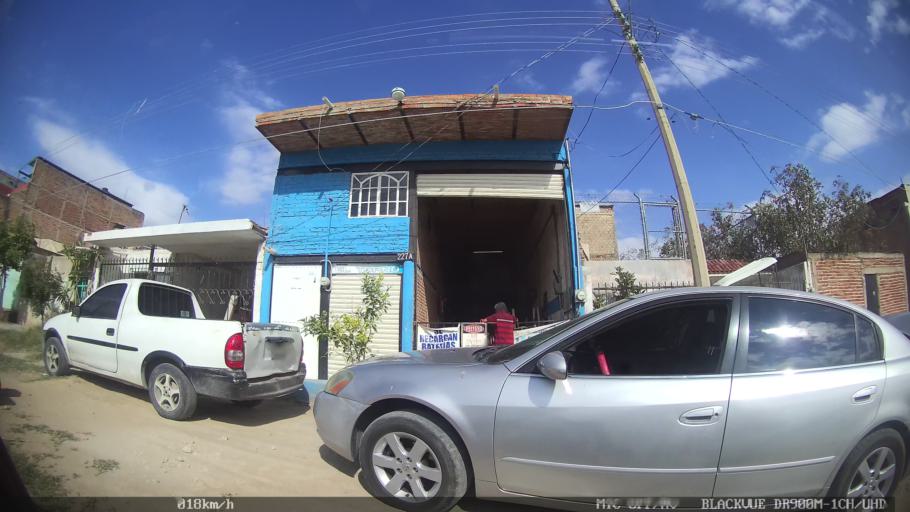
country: MX
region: Jalisco
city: Tonala
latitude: 20.6514
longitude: -103.2474
